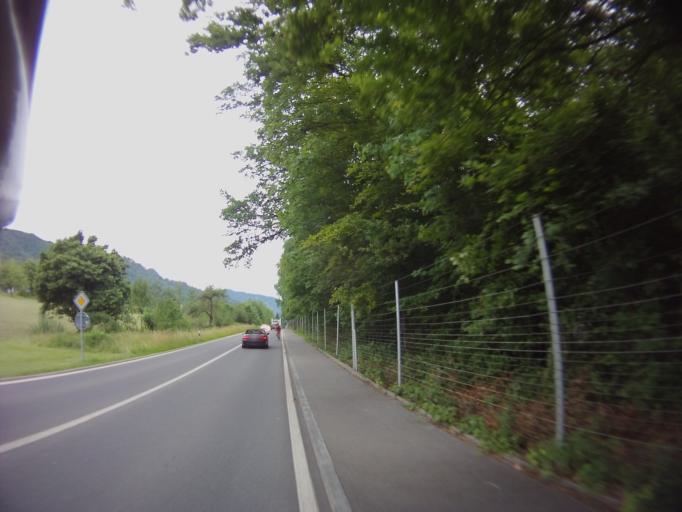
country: CH
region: Zurich
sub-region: Bezirk Horgen
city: Langnau / Vitaquartier
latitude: 47.2928
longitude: 8.5268
